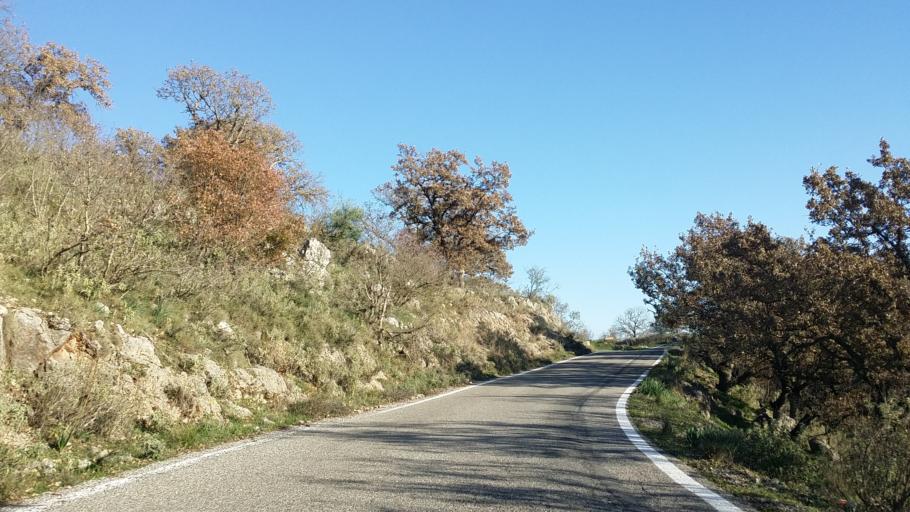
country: GR
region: West Greece
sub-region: Nomos Aitolias kai Akarnanias
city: Fitiai
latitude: 38.6354
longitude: 21.1950
